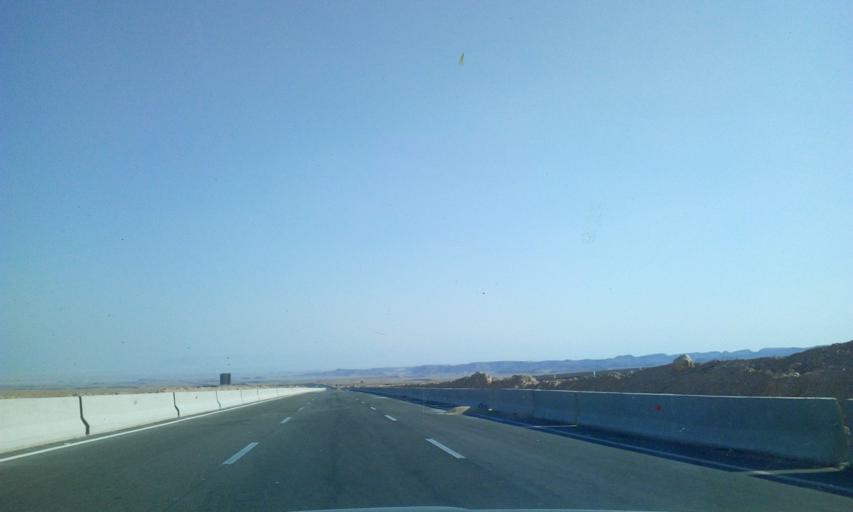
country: EG
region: As Suways
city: Ain Sukhna
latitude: 29.2834
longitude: 32.4682
